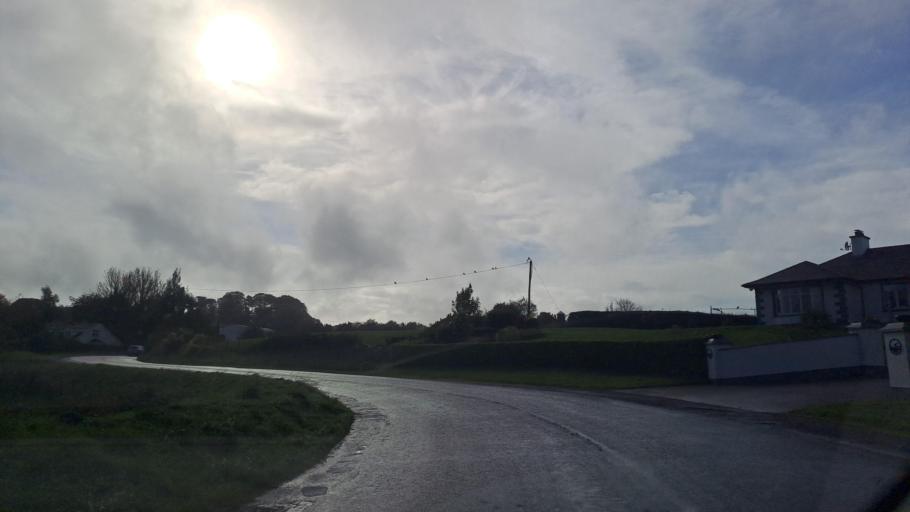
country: IE
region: Ulster
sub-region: County Monaghan
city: Carrickmacross
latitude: 53.9543
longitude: -6.7148
